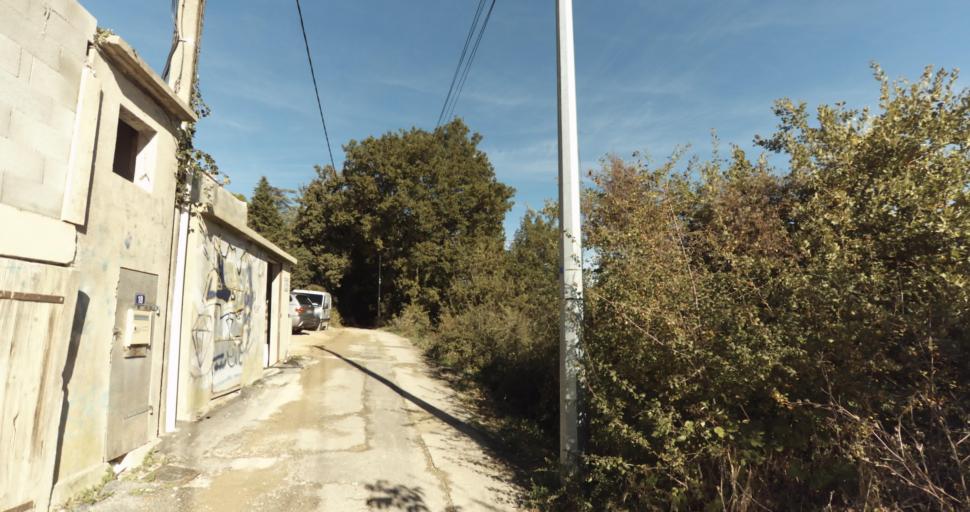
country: FR
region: Provence-Alpes-Cote d'Azur
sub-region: Departement des Bouches-du-Rhone
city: Venelles
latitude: 43.5906
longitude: 5.4752
